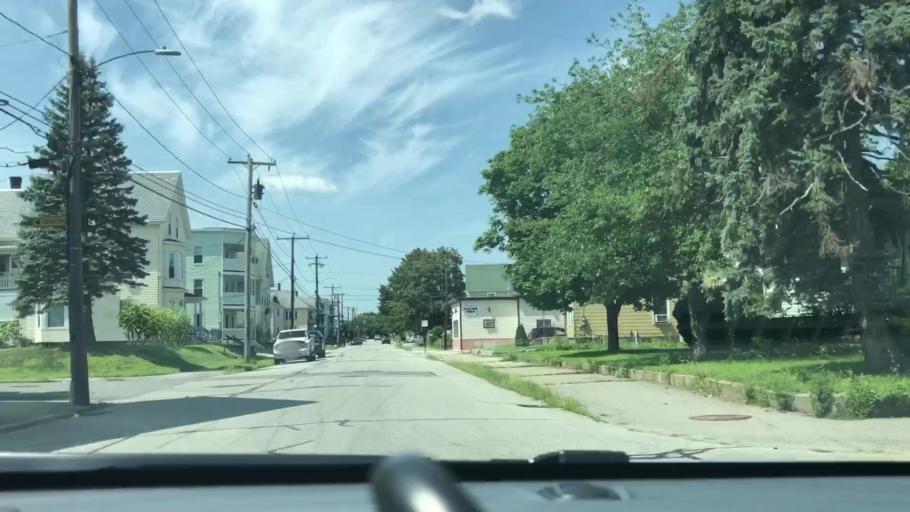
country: US
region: New Hampshire
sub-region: Hillsborough County
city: Pinardville
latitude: 42.9936
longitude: -71.4847
